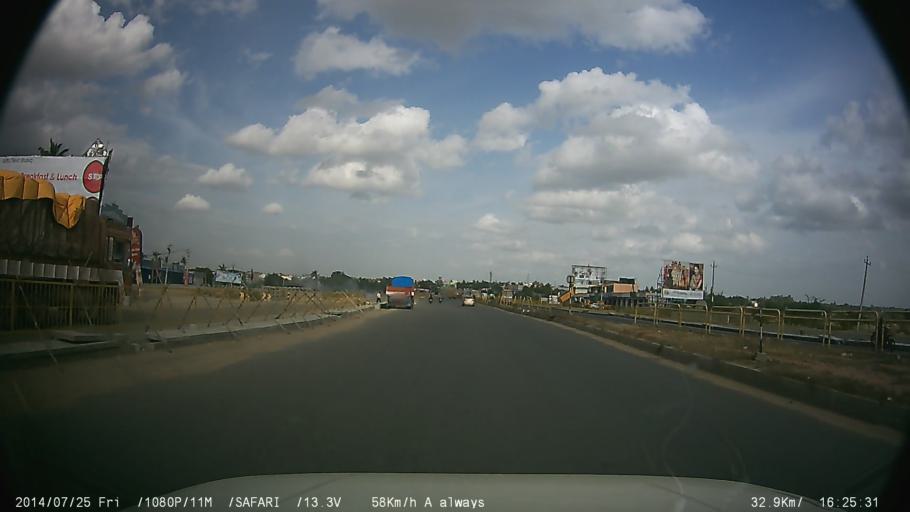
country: IN
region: Tamil Nadu
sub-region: Krishnagiri
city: Hosur
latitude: 12.7746
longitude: 77.7809
